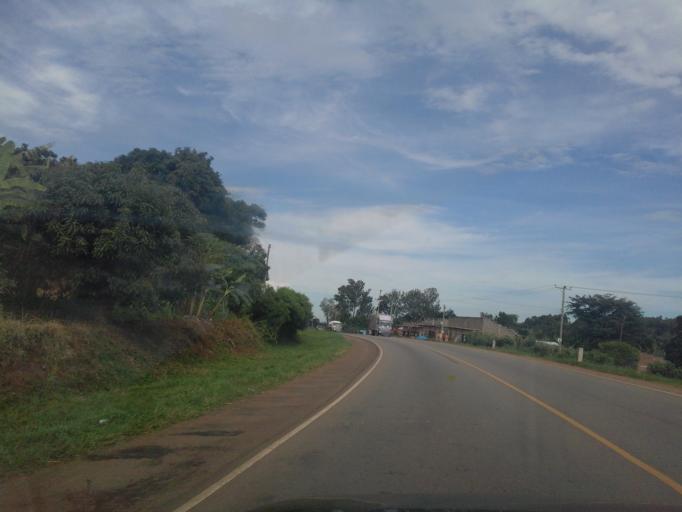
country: UG
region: Central Region
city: Masaka
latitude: -0.3454
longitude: 31.6247
